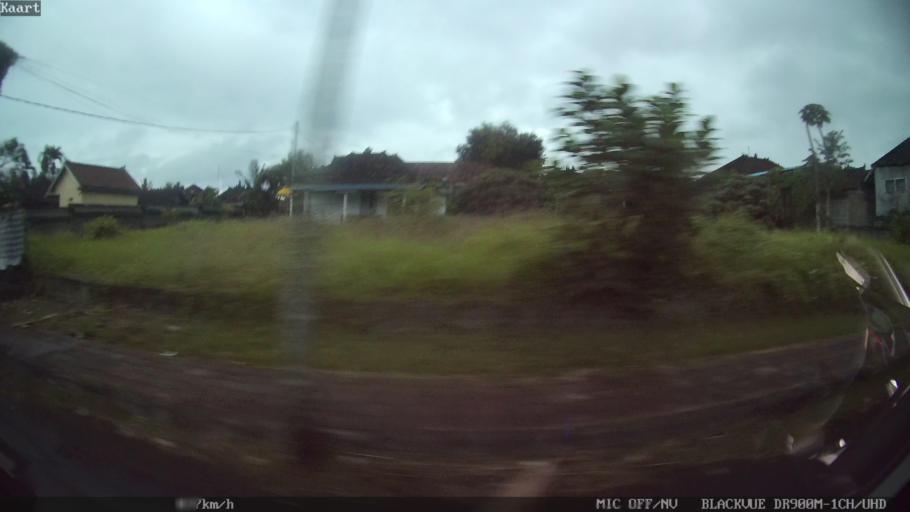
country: ID
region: Bali
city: Banjar Desa
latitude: -8.5849
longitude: 115.2786
